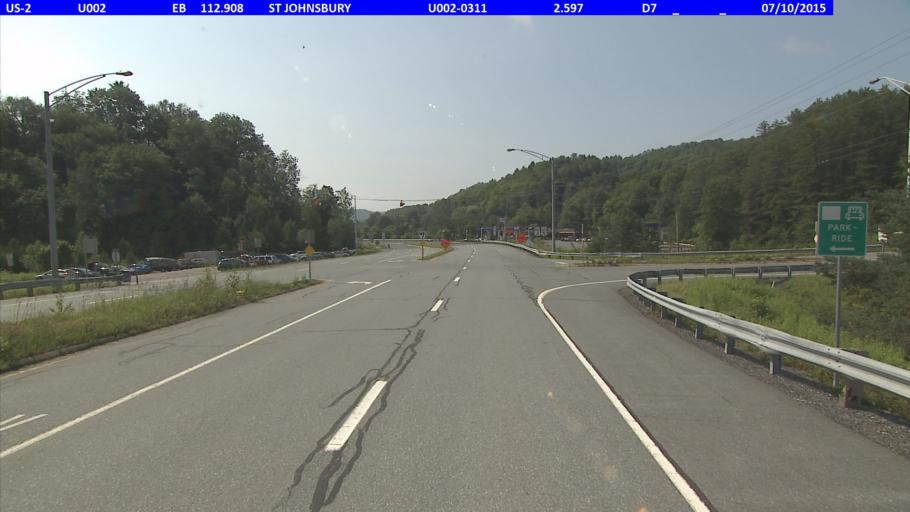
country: US
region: Vermont
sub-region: Caledonia County
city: Saint Johnsbury
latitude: 44.4204
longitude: -72.0299
